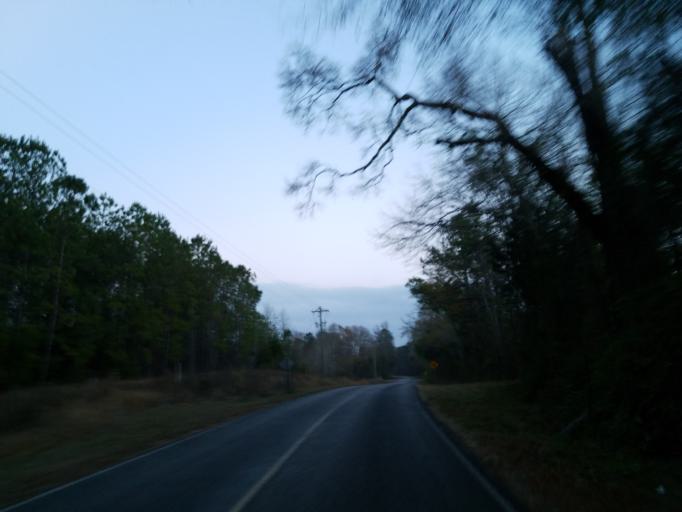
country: US
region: Alabama
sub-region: Sumter County
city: York
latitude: 32.4021
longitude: -88.4616
